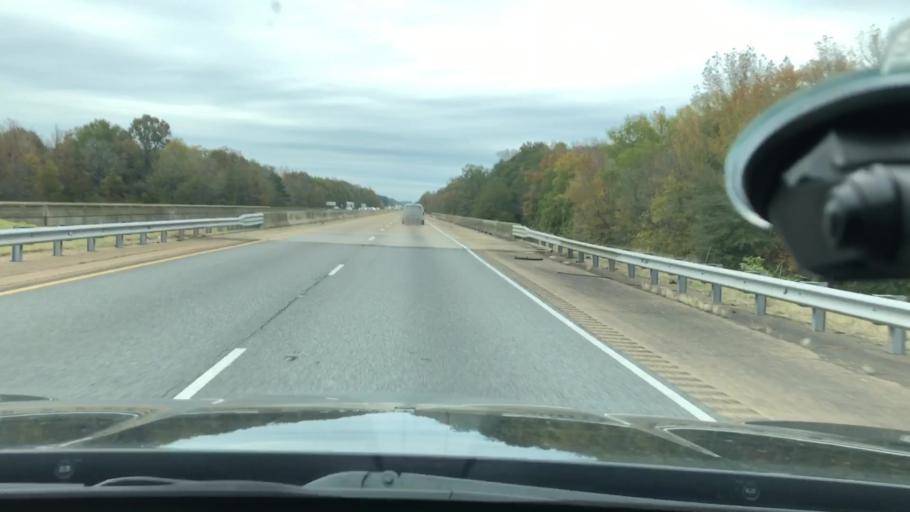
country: US
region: Arkansas
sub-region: Nevada County
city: Prescott
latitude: 33.8926
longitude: -93.3114
